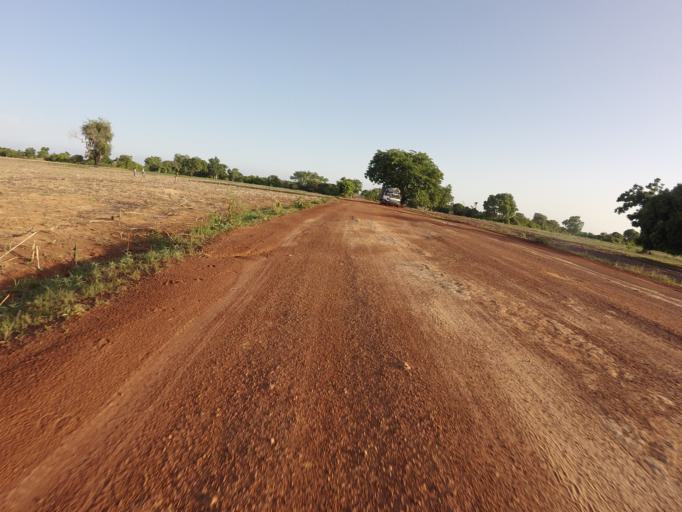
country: TG
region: Savanes
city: Sansanne-Mango
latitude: 10.3429
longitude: -0.0926
